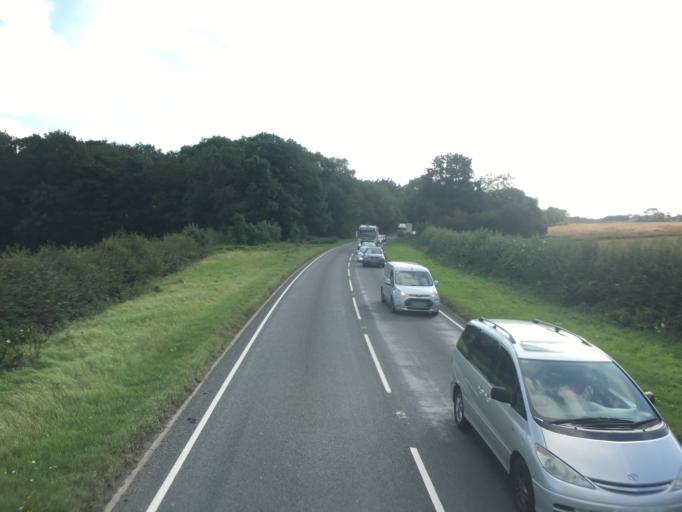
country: GB
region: England
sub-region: Leicestershire
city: Lutterworth
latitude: 52.4167
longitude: -1.2324
